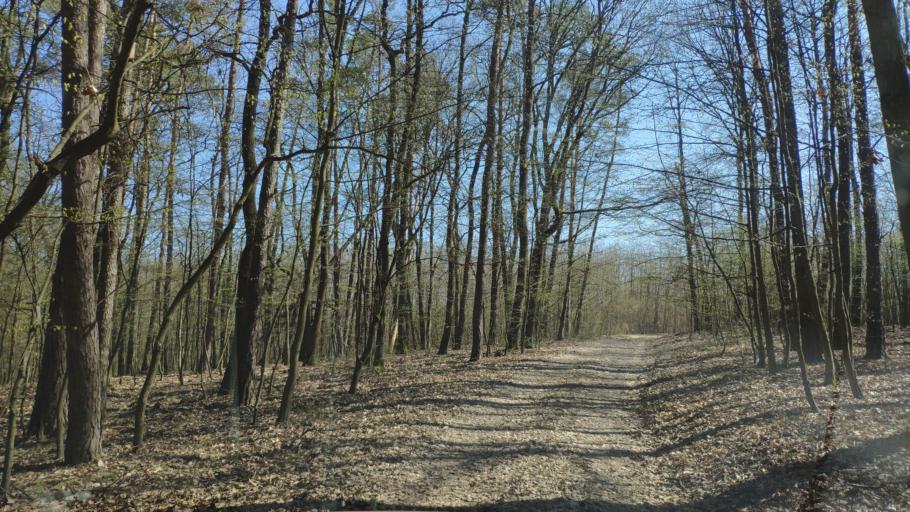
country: SK
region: Kosicky
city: Moldava nad Bodvou
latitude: 48.5630
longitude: 20.9315
